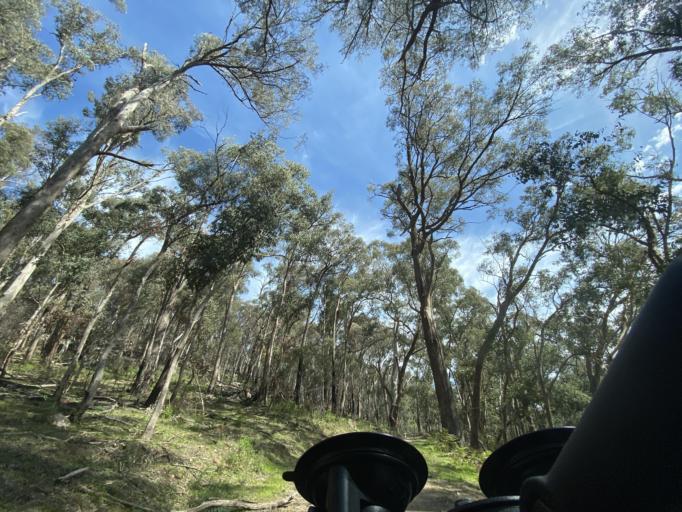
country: AU
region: Victoria
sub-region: Mansfield
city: Mansfield
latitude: -36.8337
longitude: 146.1007
